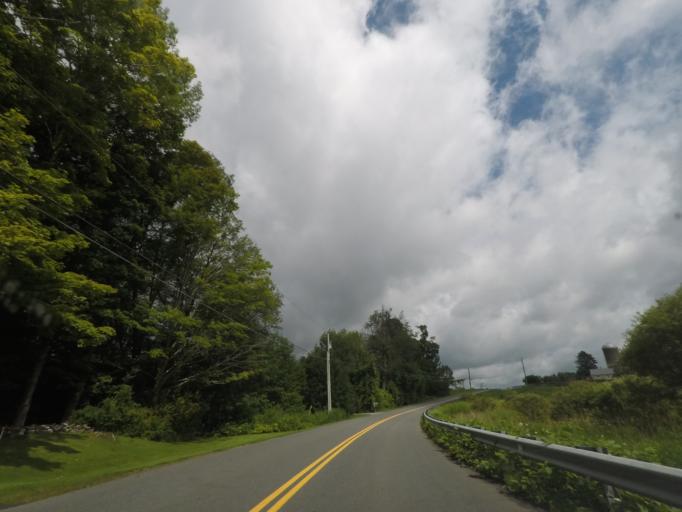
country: US
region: Massachusetts
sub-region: Berkshire County
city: Lanesborough
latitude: 42.5566
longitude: -73.2515
